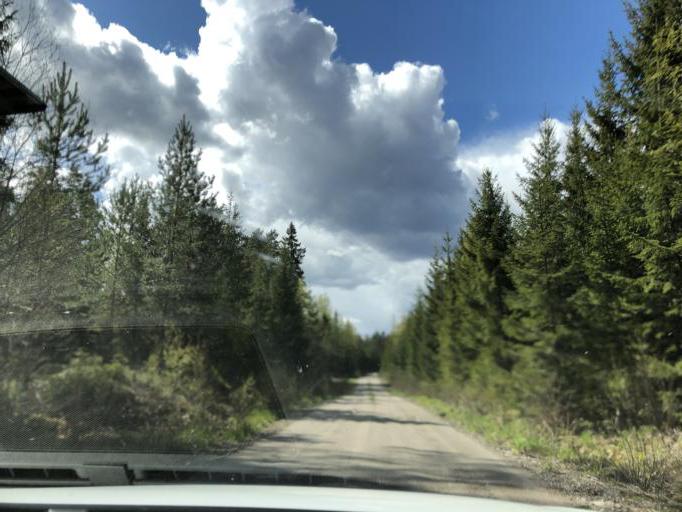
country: SE
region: Uppsala
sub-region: Heby Kommun
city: Tarnsjo
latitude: 60.2410
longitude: 16.9016
